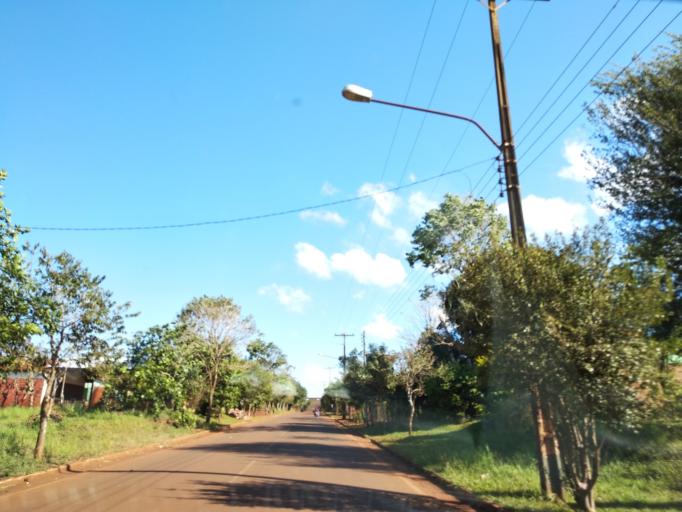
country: PY
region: Itapua
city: Hohenau
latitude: -27.0558
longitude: -55.7491
